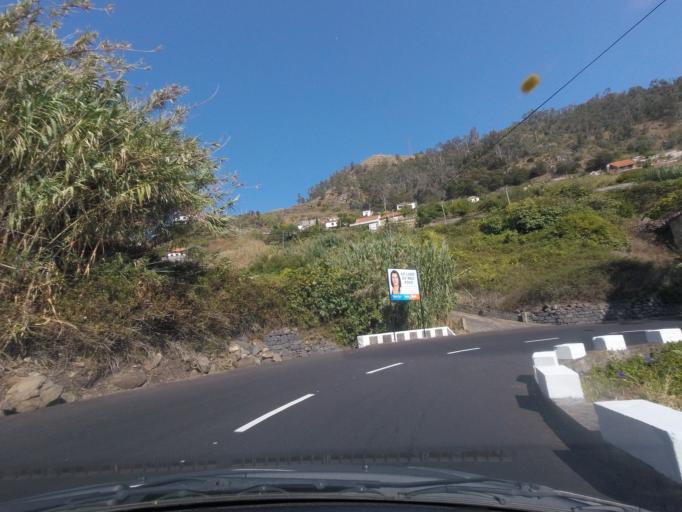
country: PT
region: Madeira
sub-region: Ribeira Brava
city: Campanario
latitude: 32.6737
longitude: -17.0383
